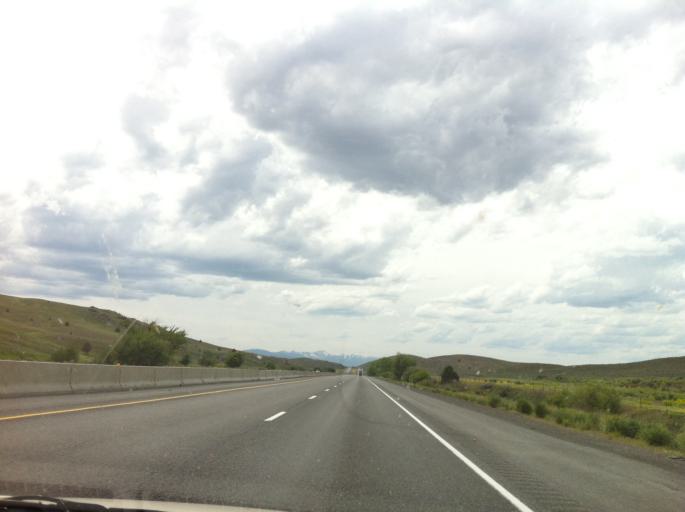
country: US
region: Oregon
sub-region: Baker County
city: Baker City
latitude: 44.5823
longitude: -117.4558
